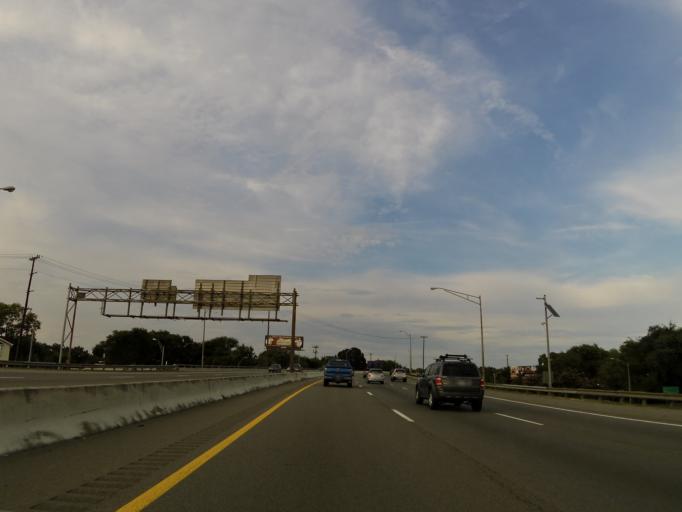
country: US
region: Tennessee
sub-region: Davidson County
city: Nashville
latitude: 36.1677
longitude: -86.8156
